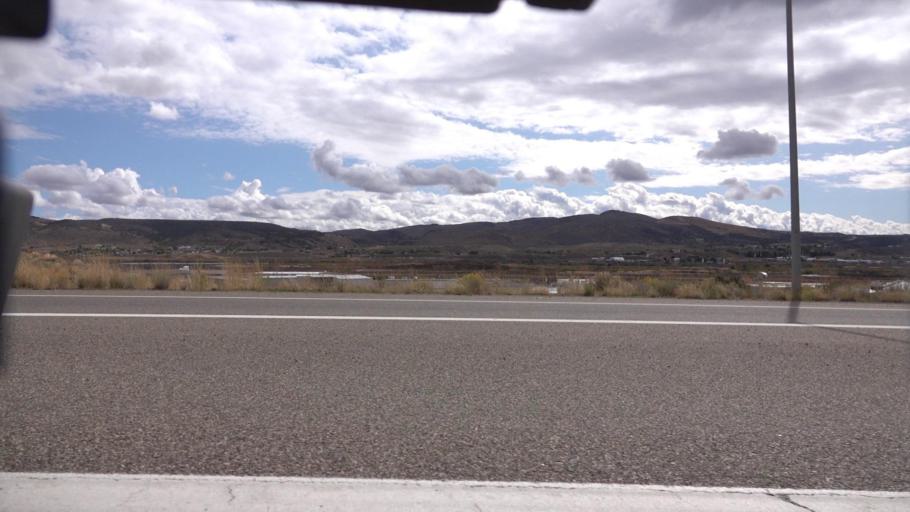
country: US
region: Nevada
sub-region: Elko County
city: Elko
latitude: 40.8553
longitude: -115.7437
